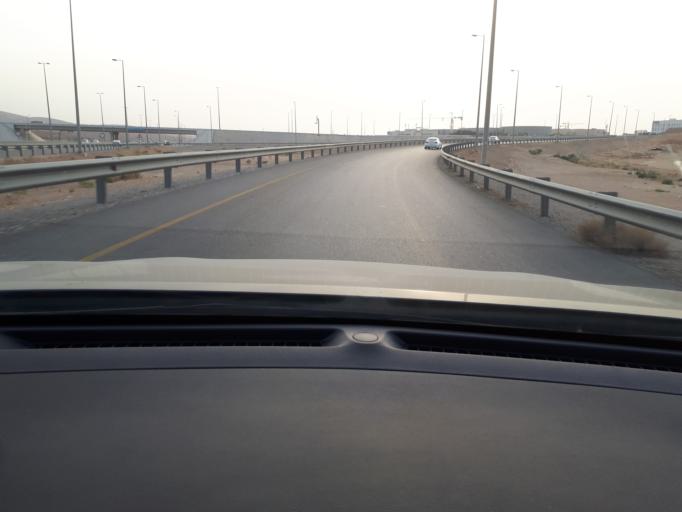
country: OM
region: Muhafazat Masqat
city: Bawshar
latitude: 23.5622
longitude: 58.3423
